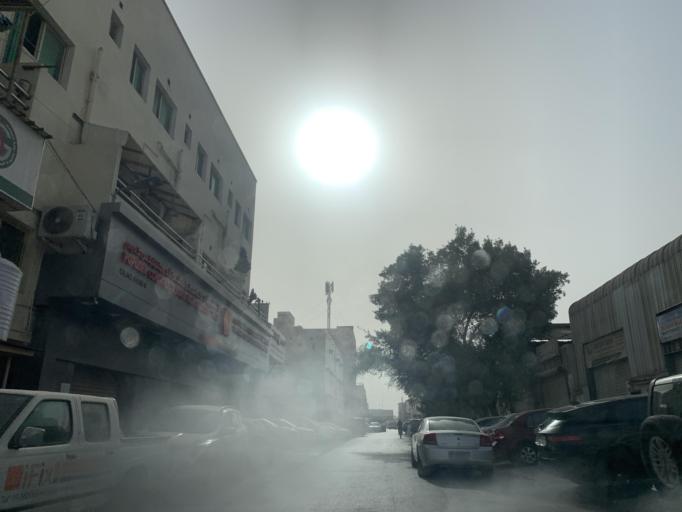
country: BH
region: Northern
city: Madinat `Isa
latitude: 26.1791
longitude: 50.5317
